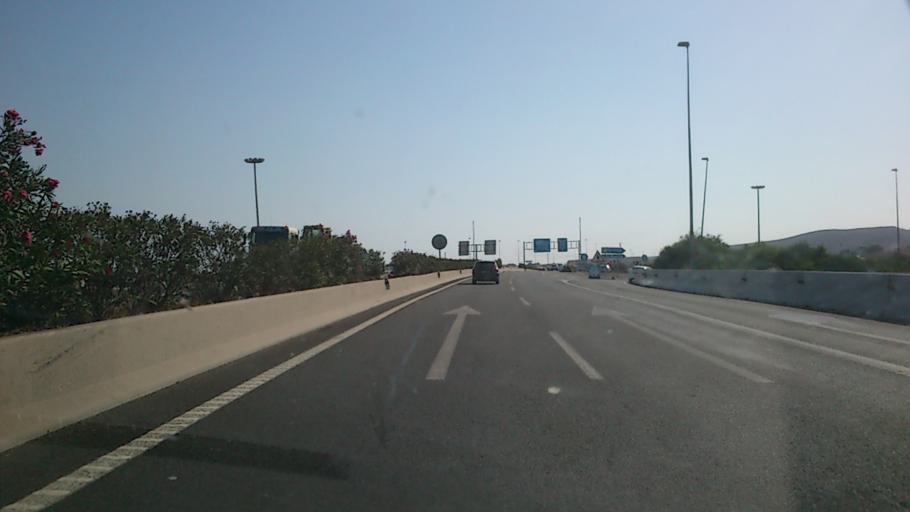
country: ES
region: Valencia
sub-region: Provincia de Alicante
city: San Vicent del Raspeig
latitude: 38.3420
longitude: -0.5430
